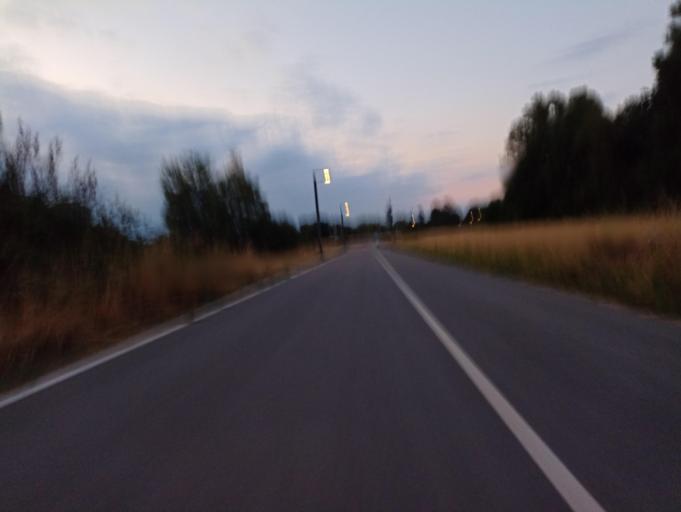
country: DE
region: Hesse
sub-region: Regierungsbezirk Darmstadt
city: Egelsbach
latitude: 49.9785
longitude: 8.6580
